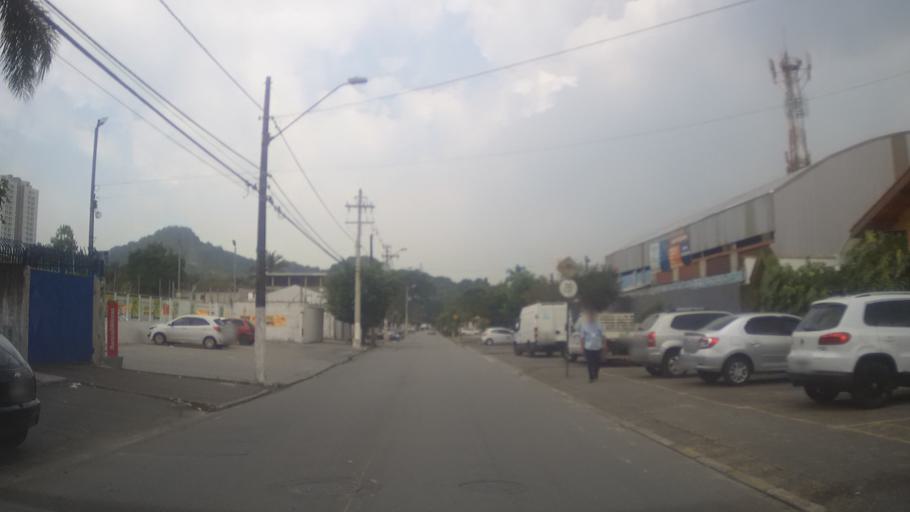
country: BR
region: Sao Paulo
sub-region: Santos
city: Santos
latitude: -23.9451
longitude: -46.3536
